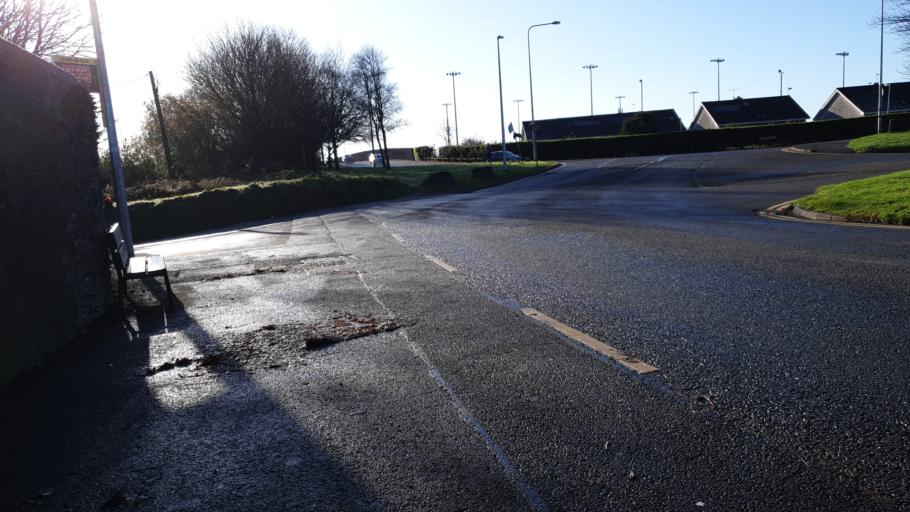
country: IE
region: Munster
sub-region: County Cork
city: Cork
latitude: 51.8921
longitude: -8.4333
